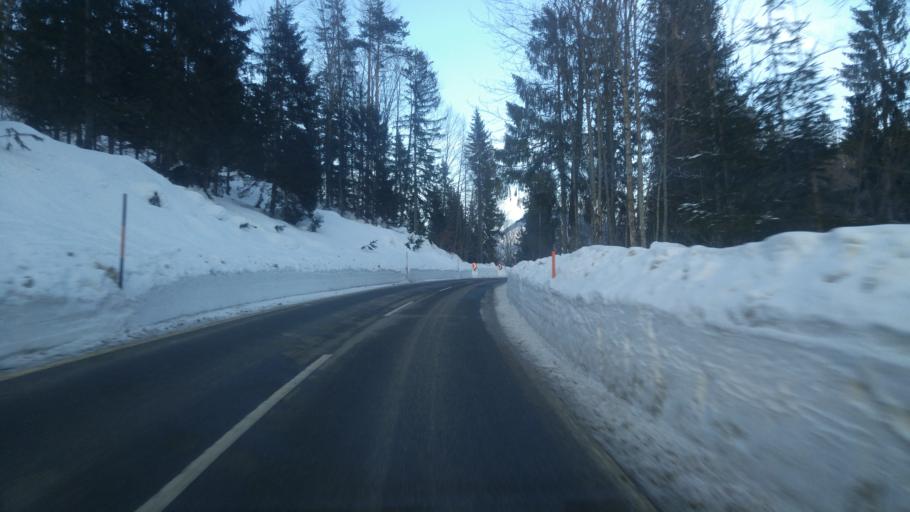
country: AT
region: Lower Austria
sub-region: Politischer Bezirk Lilienfeld
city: Hohenberg
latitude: 47.8834
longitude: 15.6402
